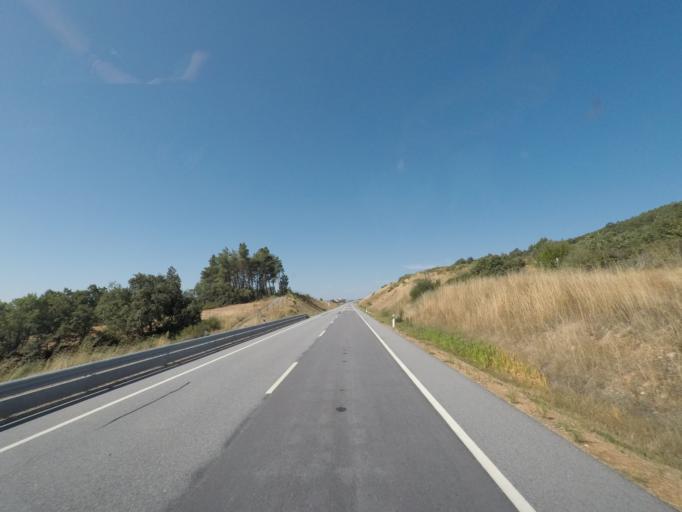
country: PT
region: Braganca
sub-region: Mogadouro
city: Mogadouro
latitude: 41.3460
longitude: -6.6209
